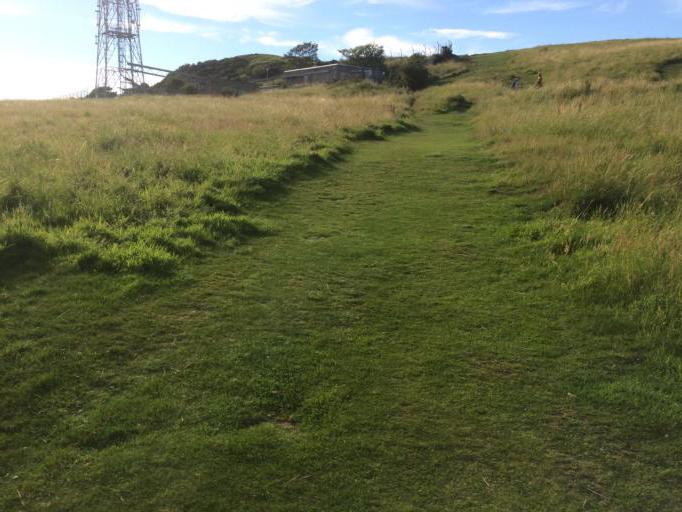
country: GB
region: Scotland
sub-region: Edinburgh
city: Edinburgh
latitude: 55.9222
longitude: -3.1922
